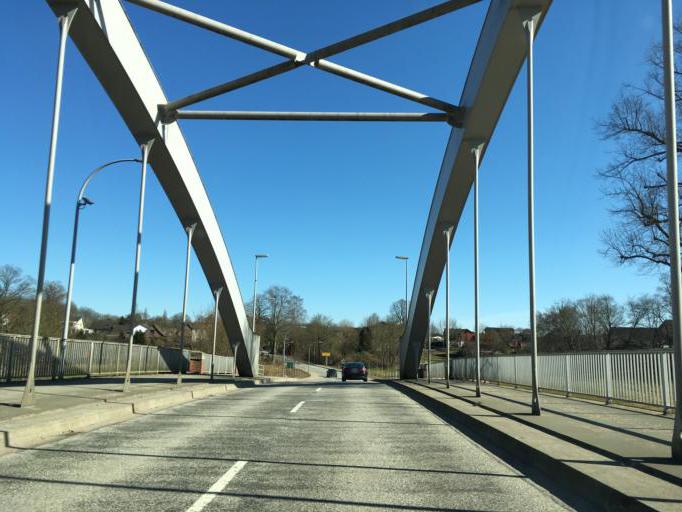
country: DE
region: Schleswig-Holstein
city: Berkenthin
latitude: 53.7339
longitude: 10.6473
